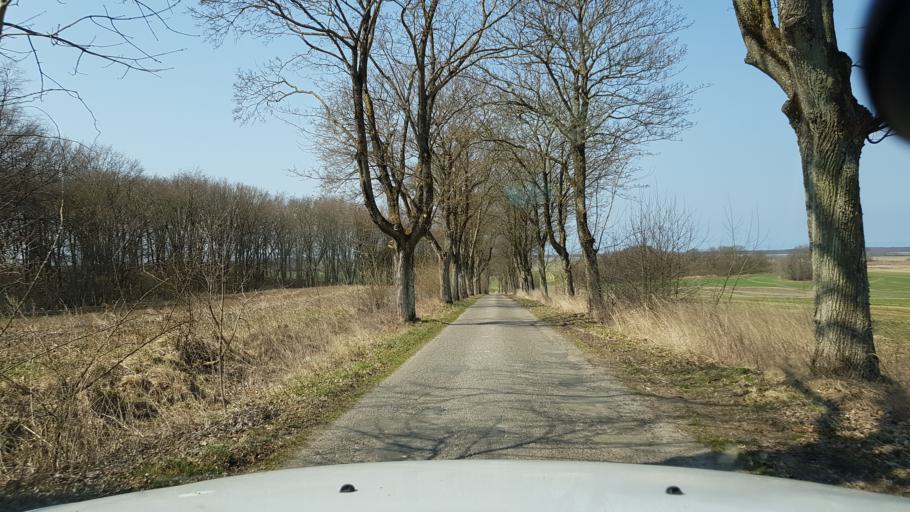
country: PL
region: West Pomeranian Voivodeship
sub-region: Powiat slawienski
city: Darlowo
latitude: 54.4670
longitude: 16.4946
